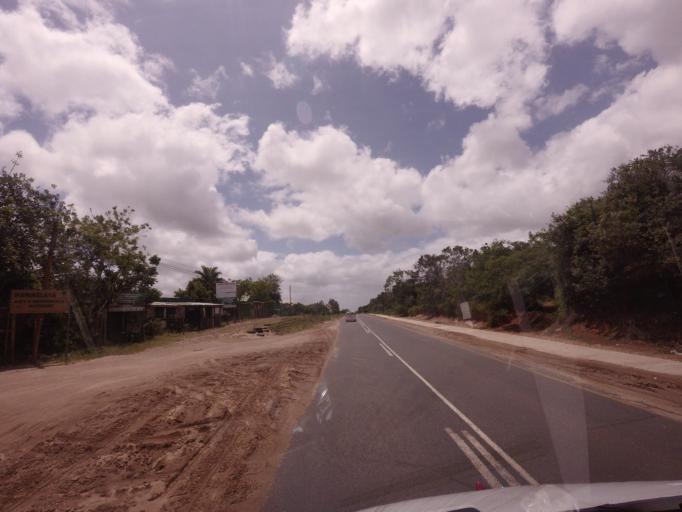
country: ZA
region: KwaZulu-Natal
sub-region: uMkhanyakude District Municipality
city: Mtubatuba
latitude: -28.3762
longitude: 32.3751
